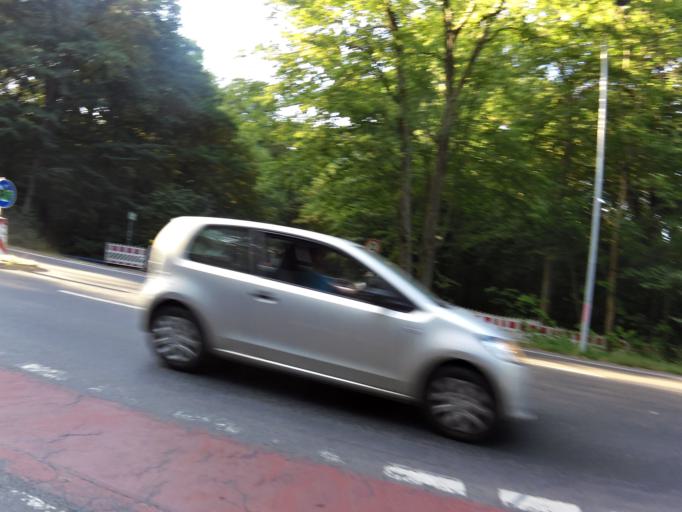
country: DE
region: Saxony
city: Leipzig
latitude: 51.3496
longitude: 12.3315
